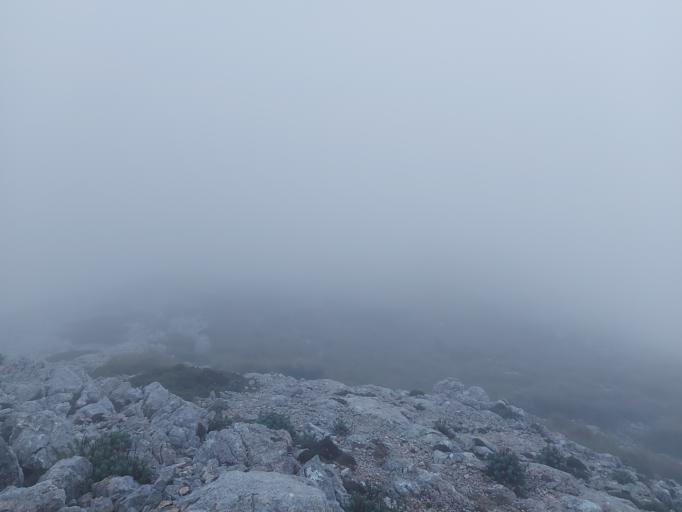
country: ES
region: Balearic Islands
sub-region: Illes Balears
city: Escorca
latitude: 39.8130
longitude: 2.8541
